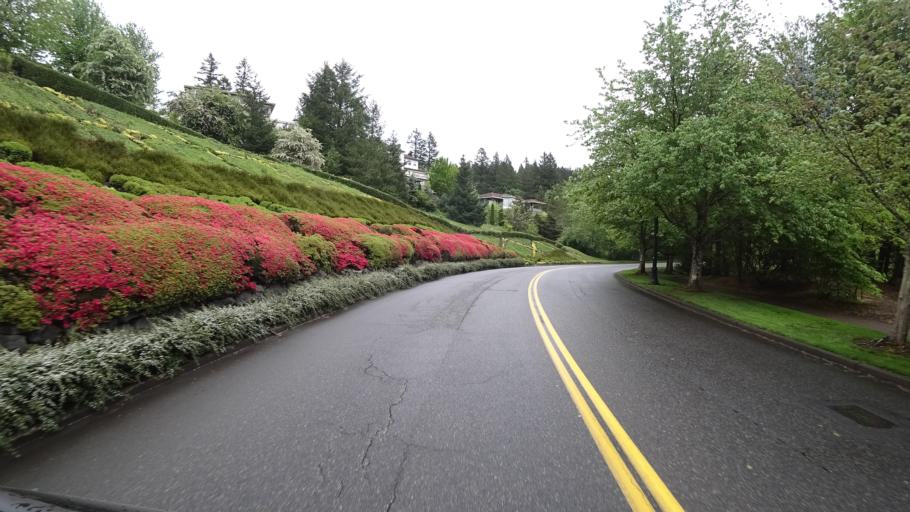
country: US
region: Oregon
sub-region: Washington County
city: West Haven
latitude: 45.5317
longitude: -122.7631
